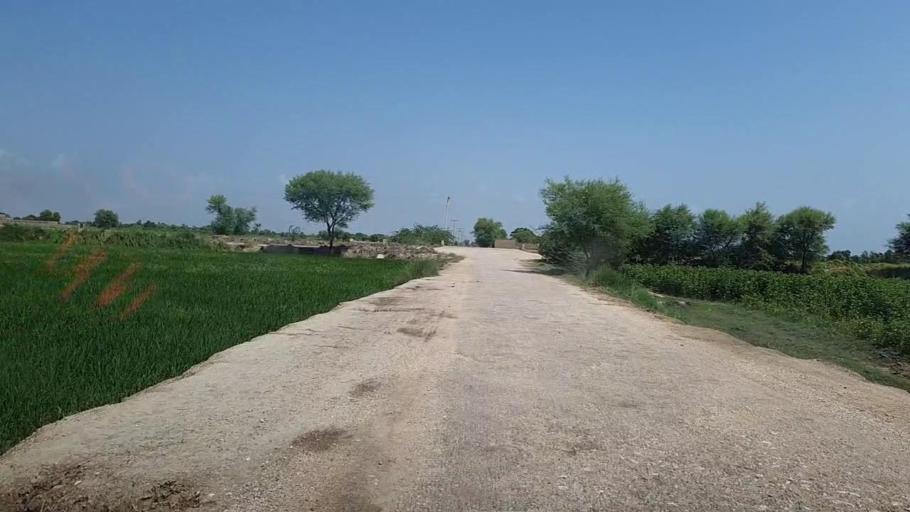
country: PK
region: Sindh
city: Bhiria
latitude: 26.8852
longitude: 68.2352
